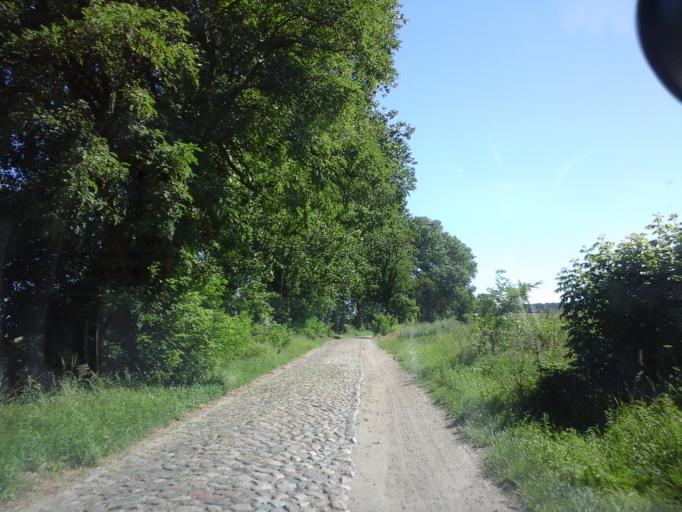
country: PL
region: West Pomeranian Voivodeship
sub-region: Powiat choszczenski
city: Choszczno
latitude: 53.1839
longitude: 15.4585
